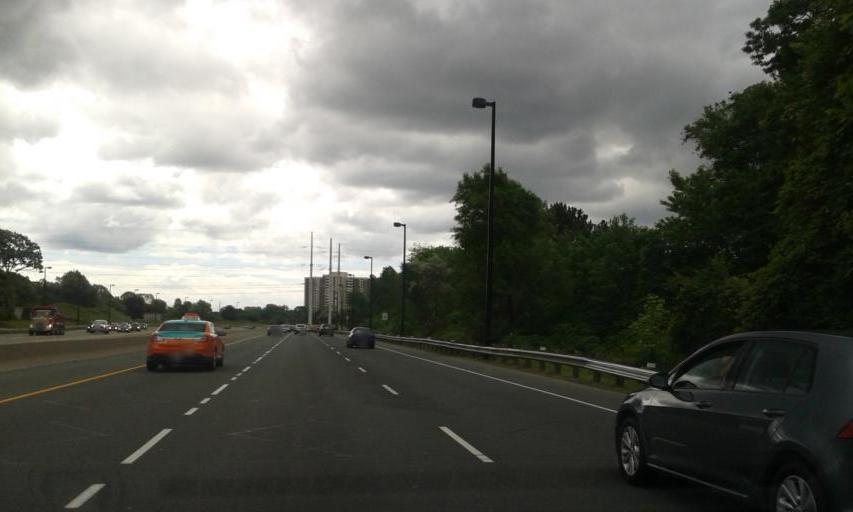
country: CA
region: Ontario
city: Willowdale
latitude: 43.7183
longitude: -79.3280
